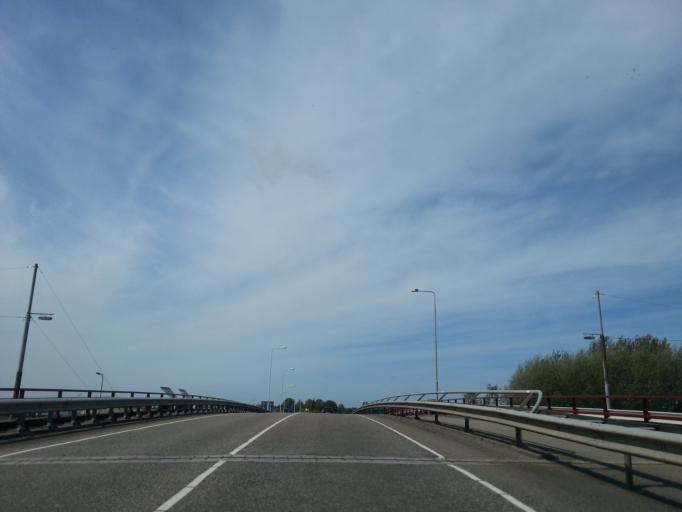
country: NL
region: North Holland
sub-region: Gemeente Beverwijk
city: Beverwijk
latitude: 52.4745
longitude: 4.6841
